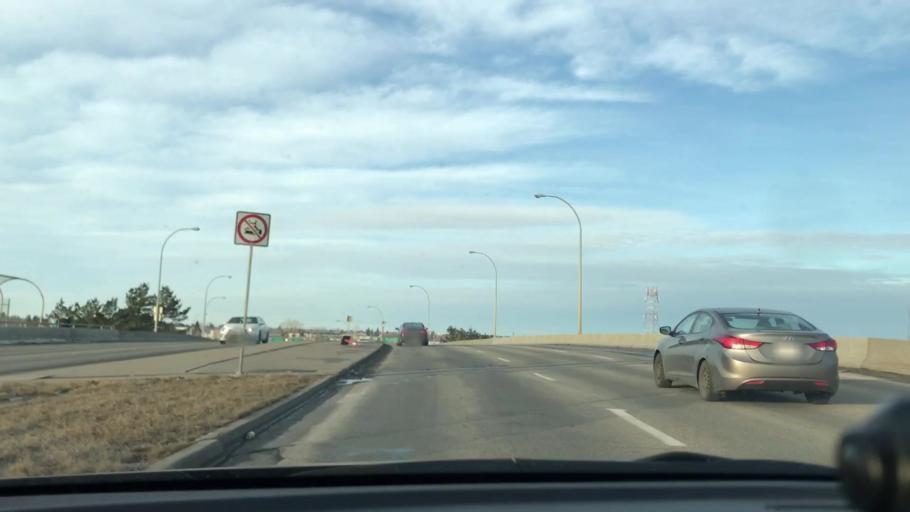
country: CA
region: Alberta
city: Edmonton
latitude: 53.5751
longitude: -113.4529
